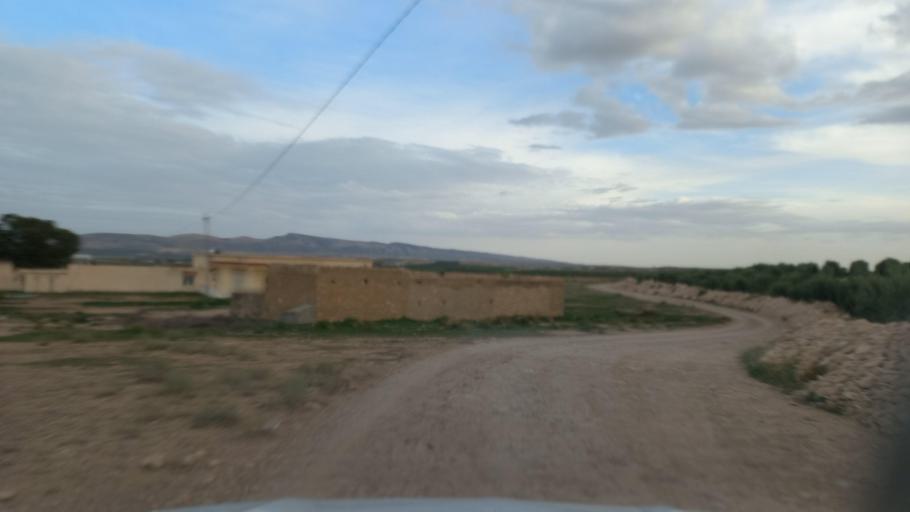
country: TN
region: Al Qasrayn
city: Sbiba
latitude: 35.4321
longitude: 9.0983
